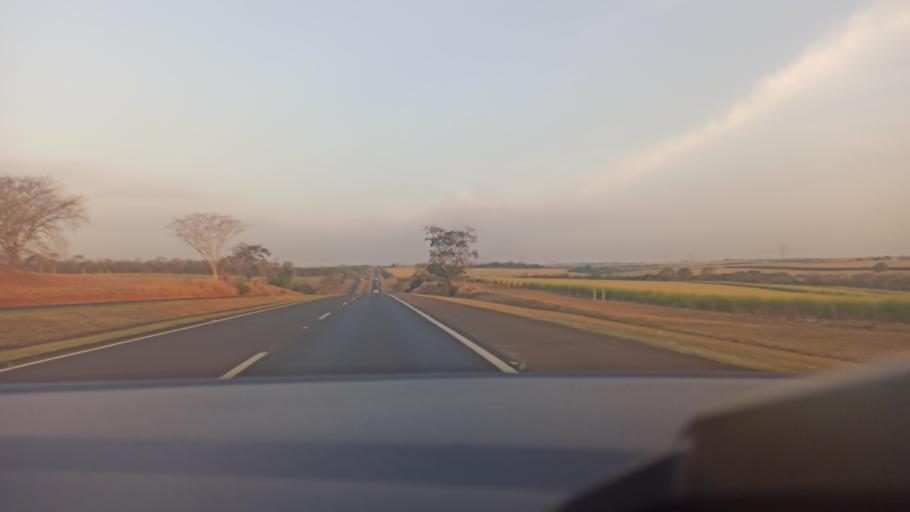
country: BR
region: Sao Paulo
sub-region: Taquaritinga
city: Taquaritinga
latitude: -21.4259
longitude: -48.6706
